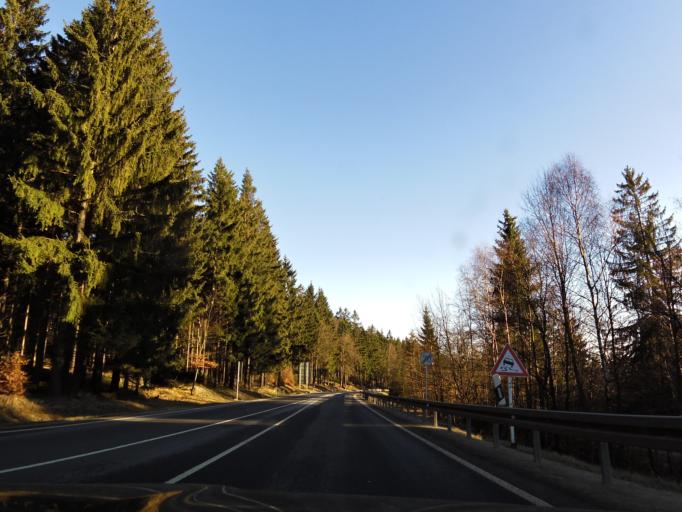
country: DE
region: Bavaria
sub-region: Upper Franconia
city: Fichtelberg
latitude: 50.0117
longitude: 11.8811
